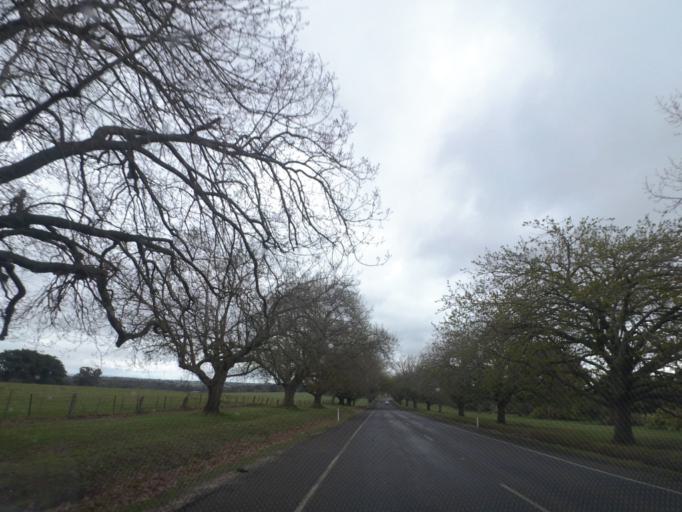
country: AU
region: Victoria
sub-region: Hume
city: Sunbury
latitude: -37.3404
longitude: 144.5279
